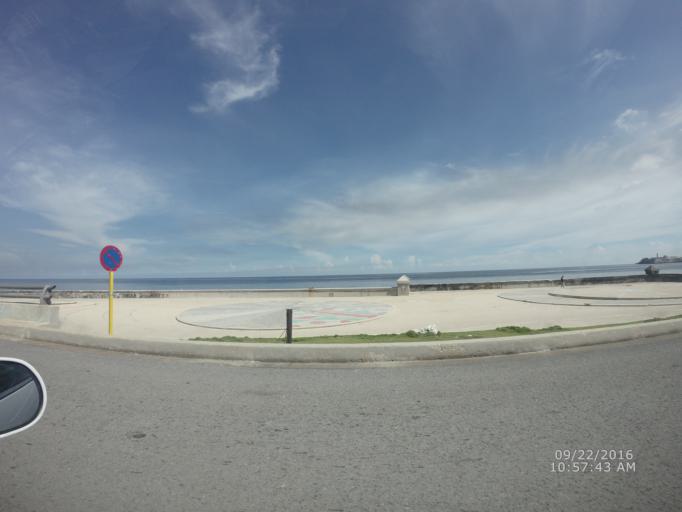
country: CU
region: La Habana
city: Centro Habana
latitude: 23.1417
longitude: -82.3715
